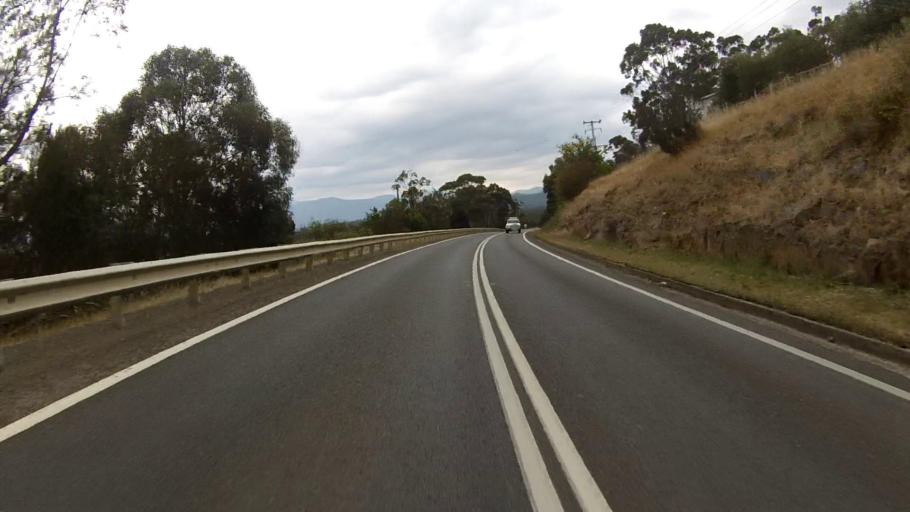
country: AU
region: Tasmania
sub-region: Huon Valley
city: Huonville
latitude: -43.0442
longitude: 147.0514
